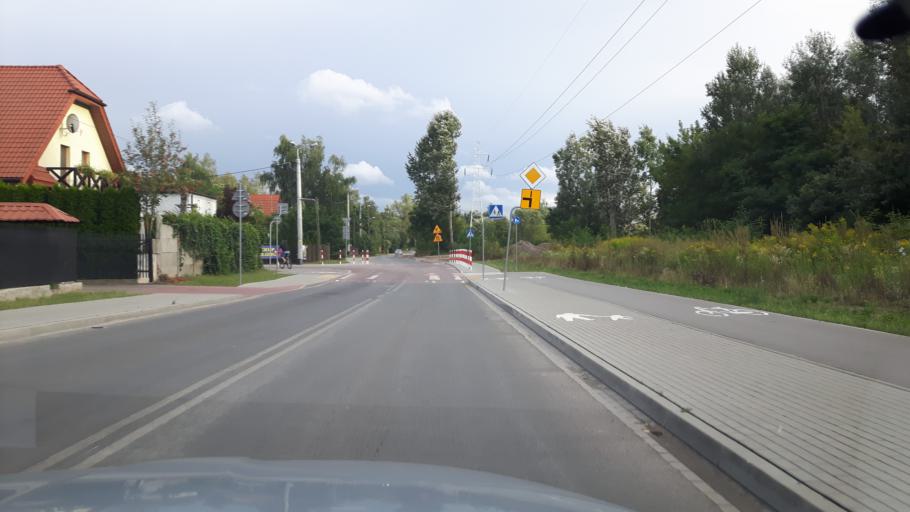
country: PL
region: Masovian Voivodeship
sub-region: Powiat wolominski
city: Marki
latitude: 52.3287
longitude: 21.1271
